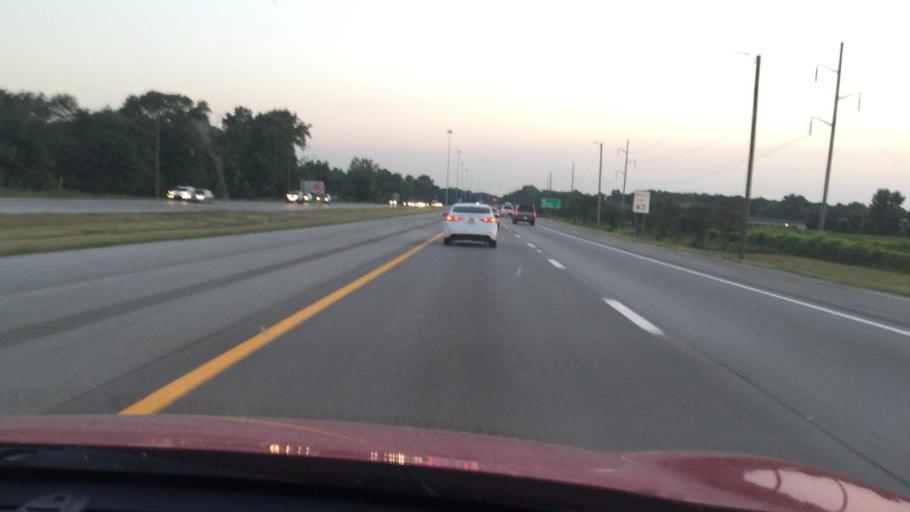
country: US
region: Ohio
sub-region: Lucas County
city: Holland
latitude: 41.6261
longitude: -83.6927
